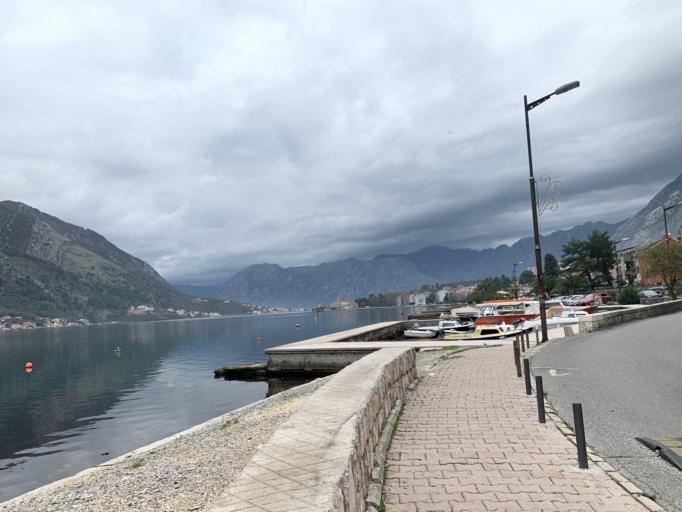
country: ME
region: Kotor
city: Kotor
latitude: 42.4304
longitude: 18.7676
